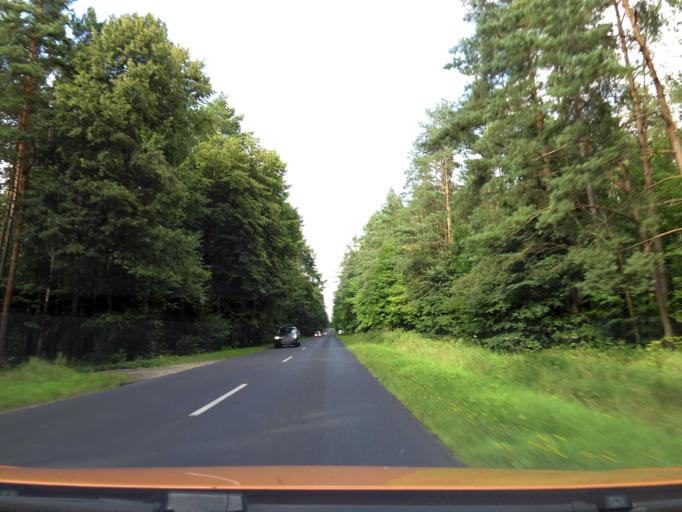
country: PL
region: West Pomeranian Voivodeship
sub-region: Powiat kolobrzeski
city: Kolobrzeg
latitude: 54.1059
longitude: 15.5829
